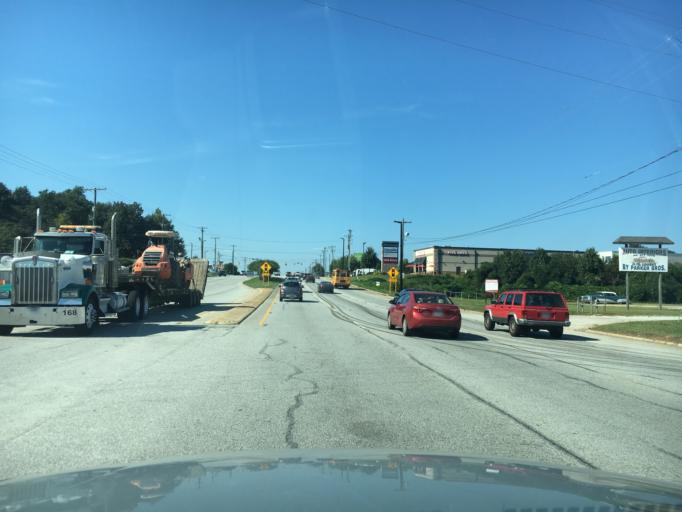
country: US
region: South Carolina
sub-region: Greenville County
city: Taylors
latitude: 34.9381
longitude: -82.2702
